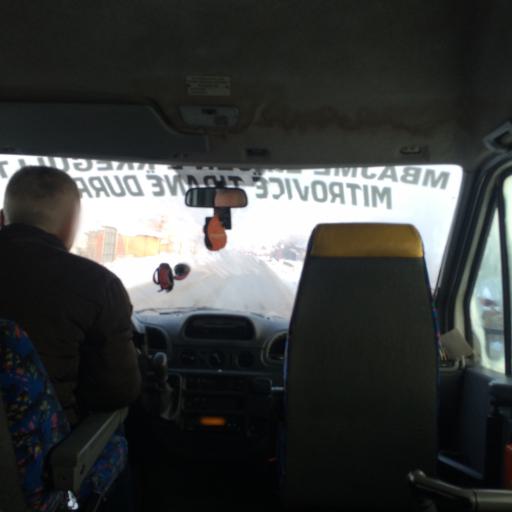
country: XK
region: Pristina
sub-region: Komuna e Drenasit
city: Glogovac
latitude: 42.5947
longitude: 20.8927
